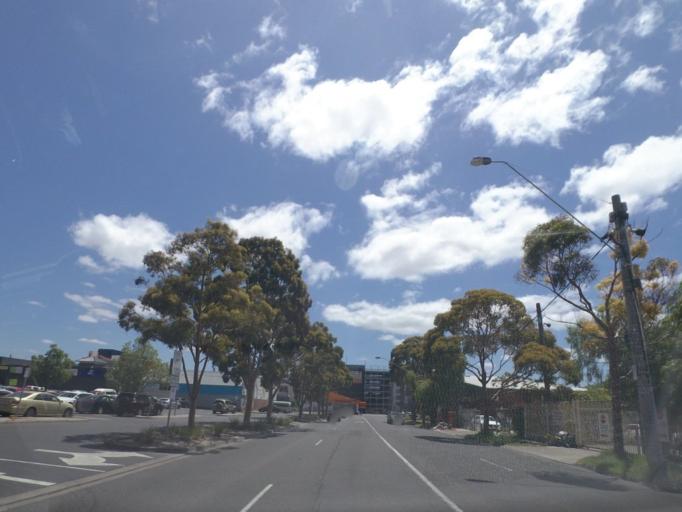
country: AU
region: Victoria
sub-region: Brimbank
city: Sunshine North
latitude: -37.7861
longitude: 144.8338
